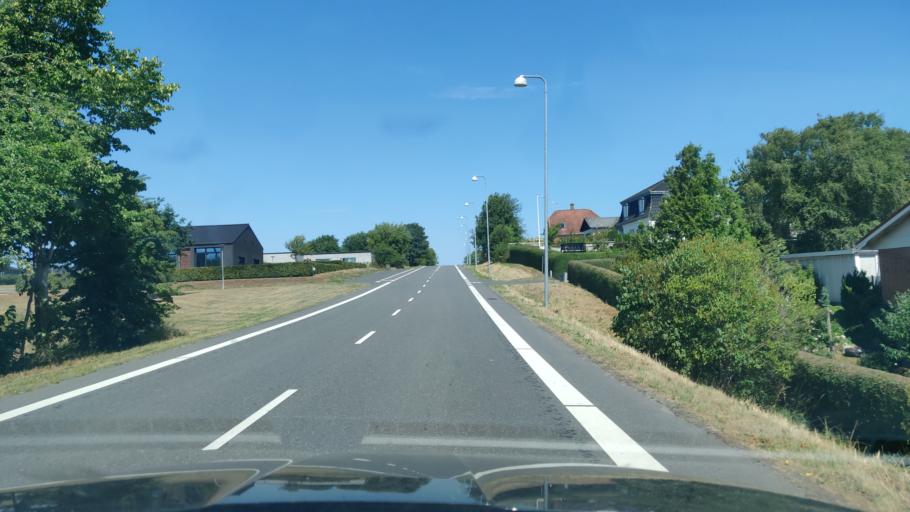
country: DK
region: South Denmark
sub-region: Kolding Kommune
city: Kolding
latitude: 55.5093
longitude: 9.5102
